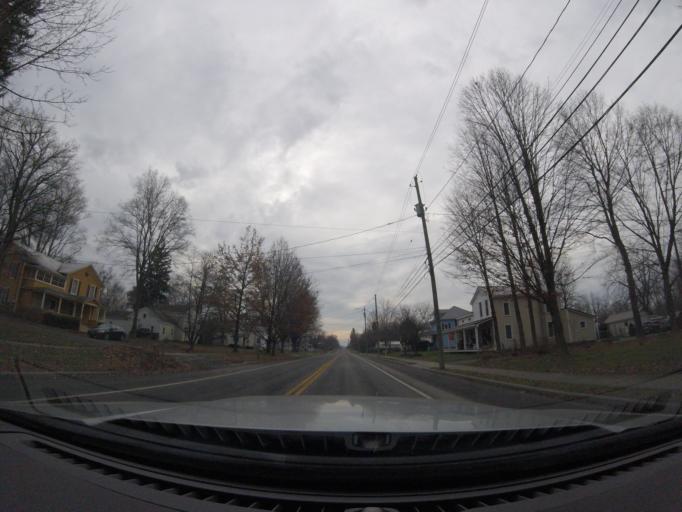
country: US
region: New York
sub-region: Schuyler County
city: Watkins Glen
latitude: 42.4165
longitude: -76.8498
